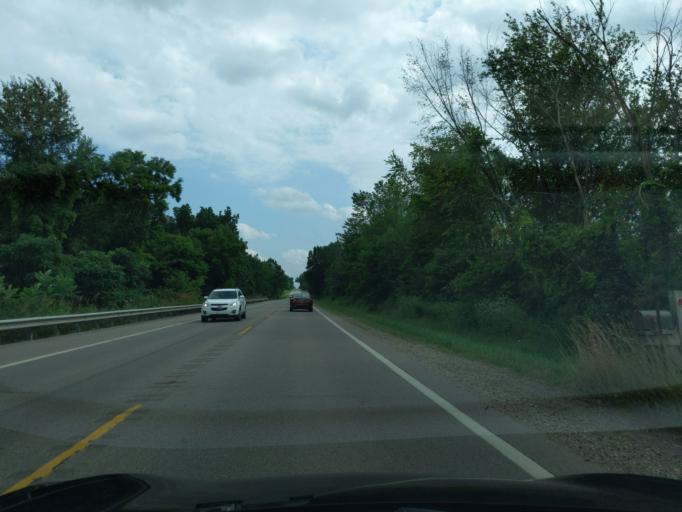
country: US
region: Michigan
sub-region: Eaton County
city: Eaton Rapids
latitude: 42.4437
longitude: -84.6497
